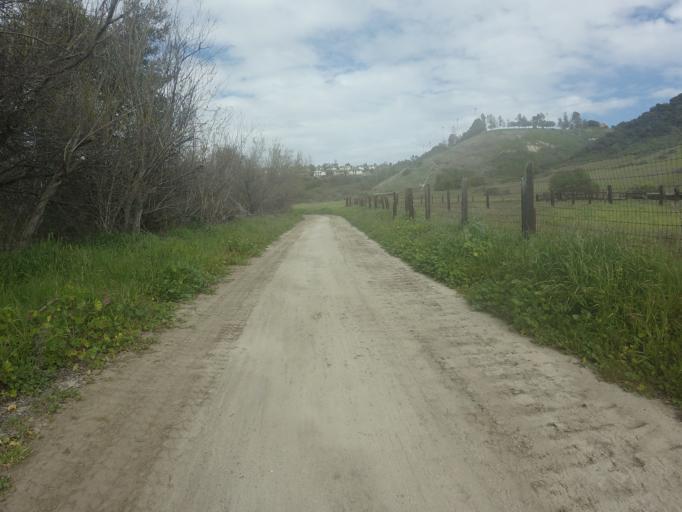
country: US
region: California
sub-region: Orange County
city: Aliso Viejo
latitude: 33.5568
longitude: -117.7403
